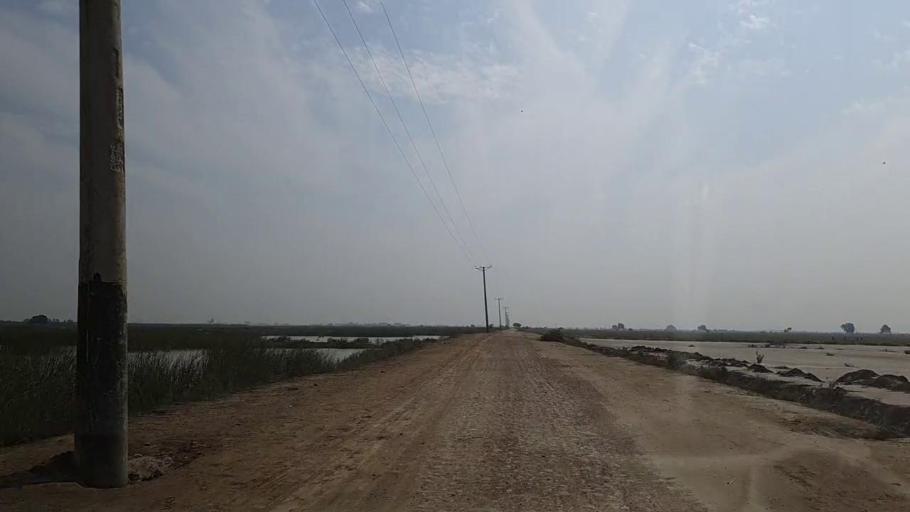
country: PK
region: Sindh
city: Mirpur Batoro
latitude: 24.6075
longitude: 68.2097
